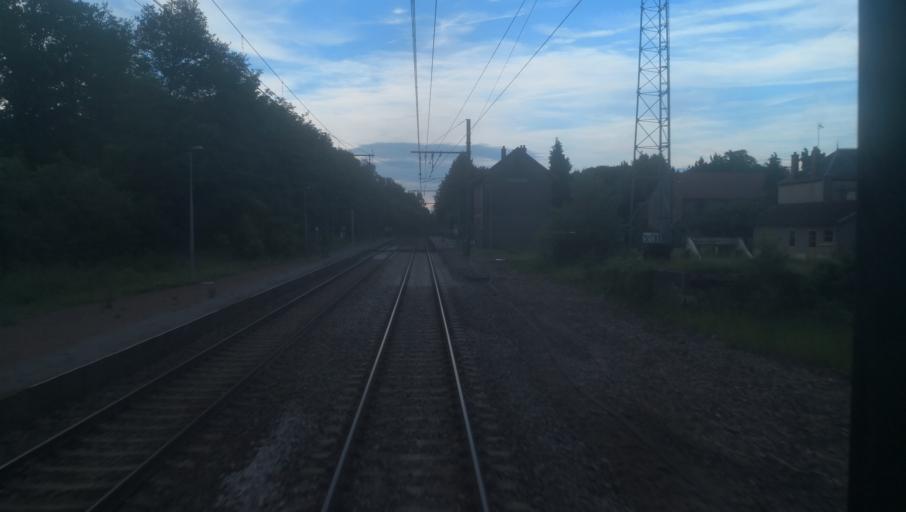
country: FR
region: Limousin
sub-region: Departement de la Creuse
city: Saint-Maurice-la-Souterraine
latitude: 46.1708
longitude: 1.4316
